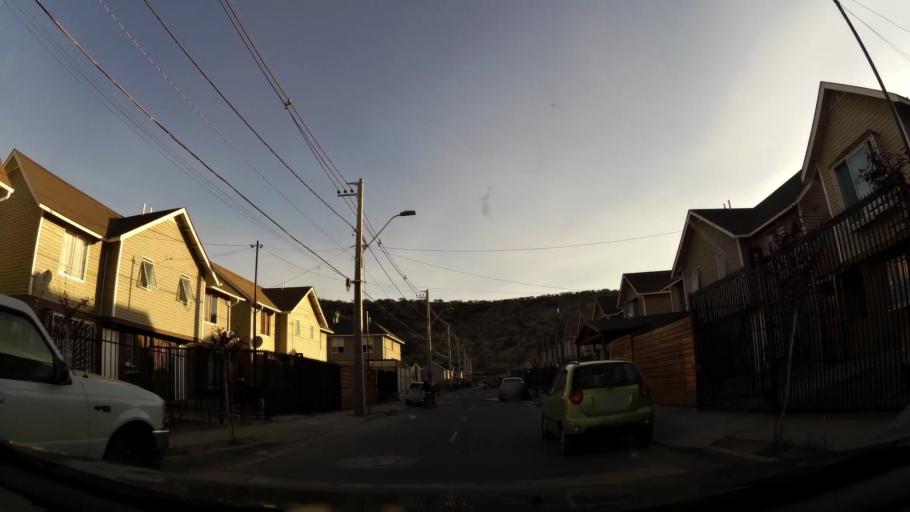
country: CL
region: Santiago Metropolitan
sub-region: Provincia de Cordillera
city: Puente Alto
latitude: -33.6010
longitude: -70.5476
